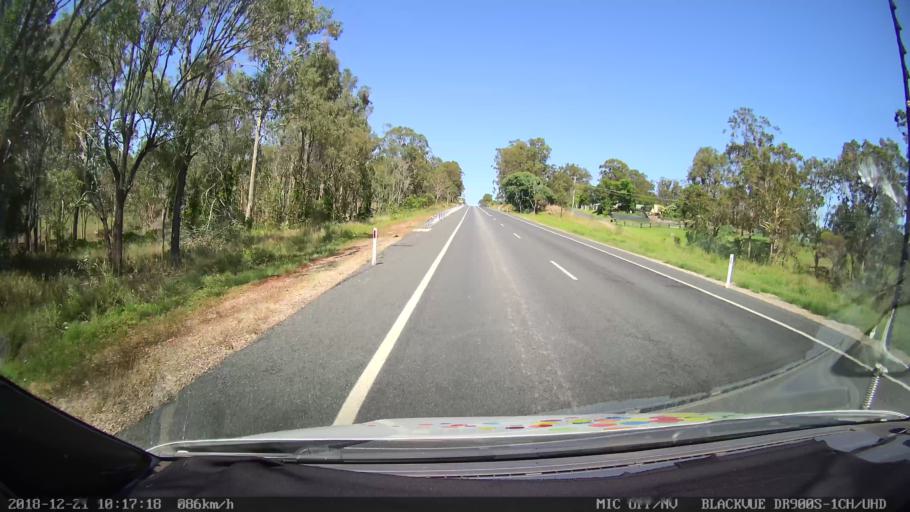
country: AU
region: New South Wales
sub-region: Clarence Valley
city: South Grafton
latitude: -29.6836
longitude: 152.8725
